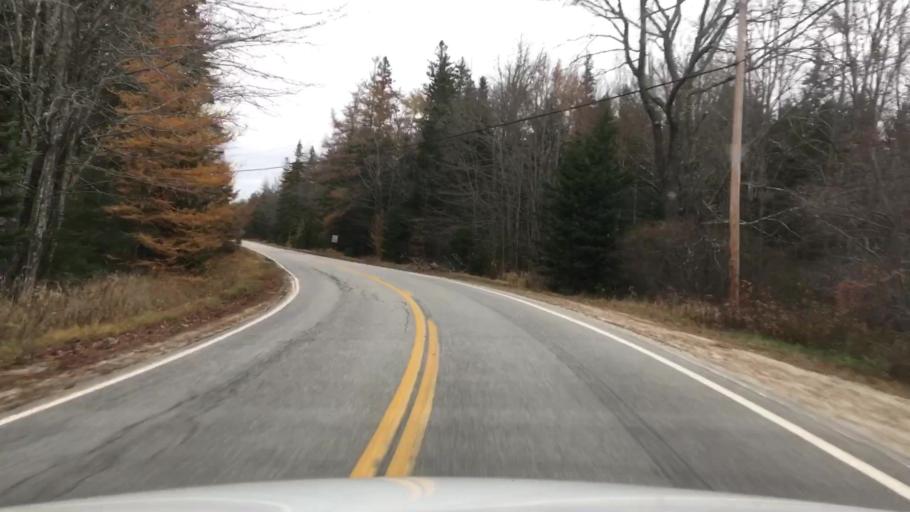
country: US
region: Maine
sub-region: Hancock County
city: Sedgwick
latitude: 44.2781
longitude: -68.5536
